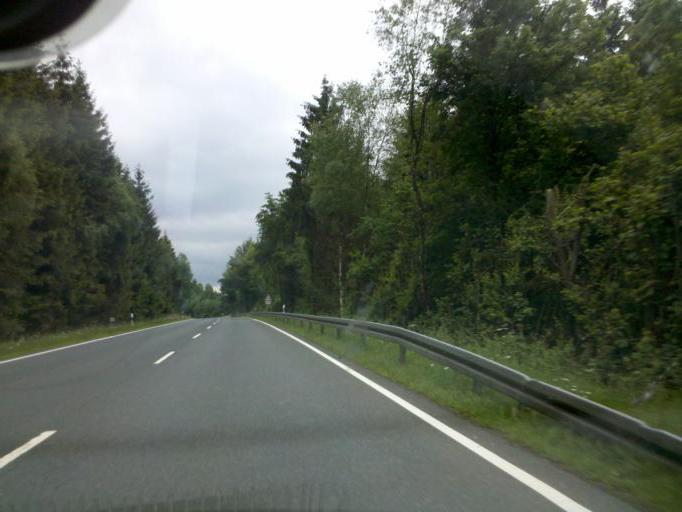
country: DE
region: North Rhine-Westphalia
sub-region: Regierungsbezirk Arnsberg
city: Wilnsdorf
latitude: 50.7837
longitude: 8.1469
